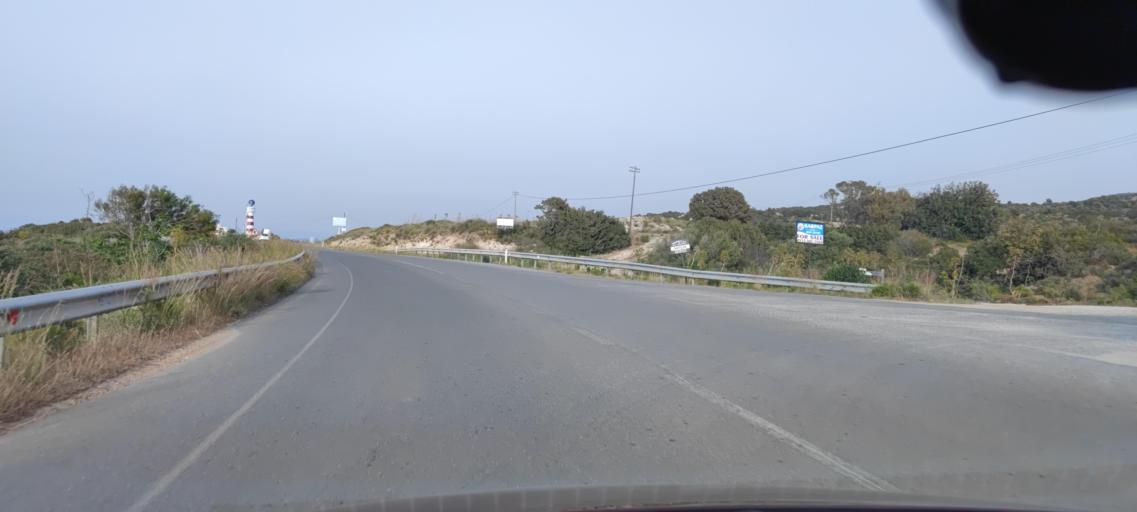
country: CY
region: Ammochostos
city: Leonarisso
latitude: 35.5555
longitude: 34.2284
